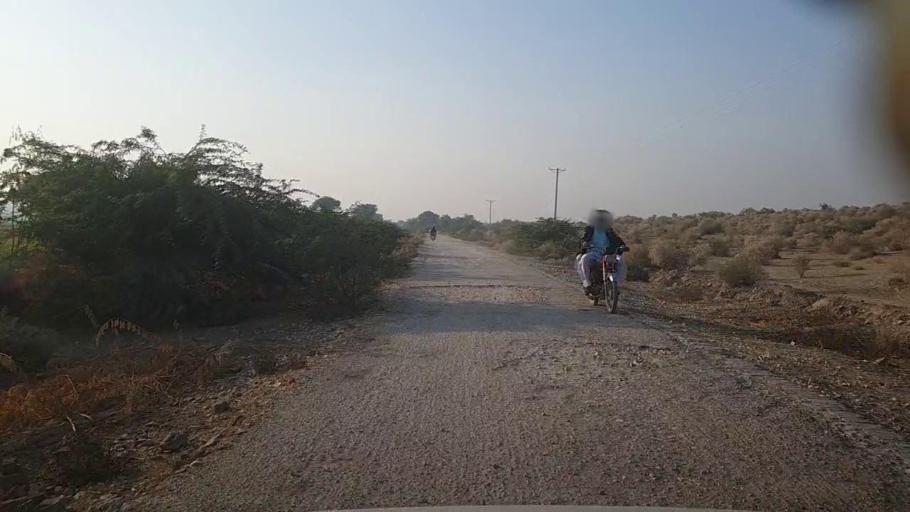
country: PK
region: Sindh
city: Pad Idan
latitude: 26.7208
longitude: 68.4545
